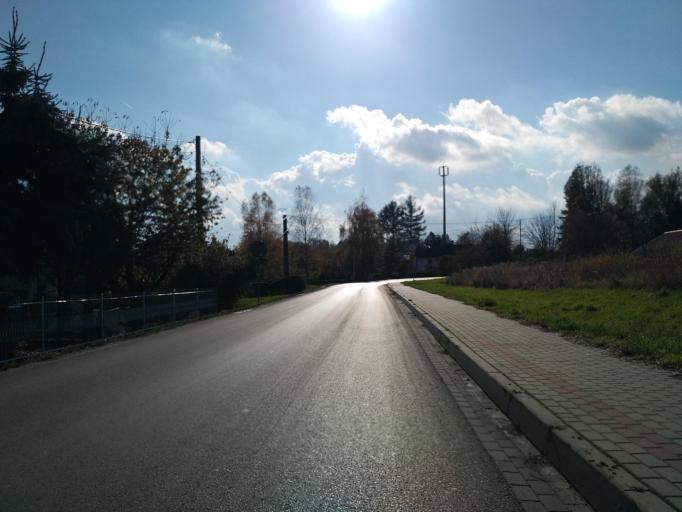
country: PL
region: Subcarpathian Voivodeship
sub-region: Powiat rzeszowski
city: Trzciana
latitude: 50.0803
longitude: 21.8394
